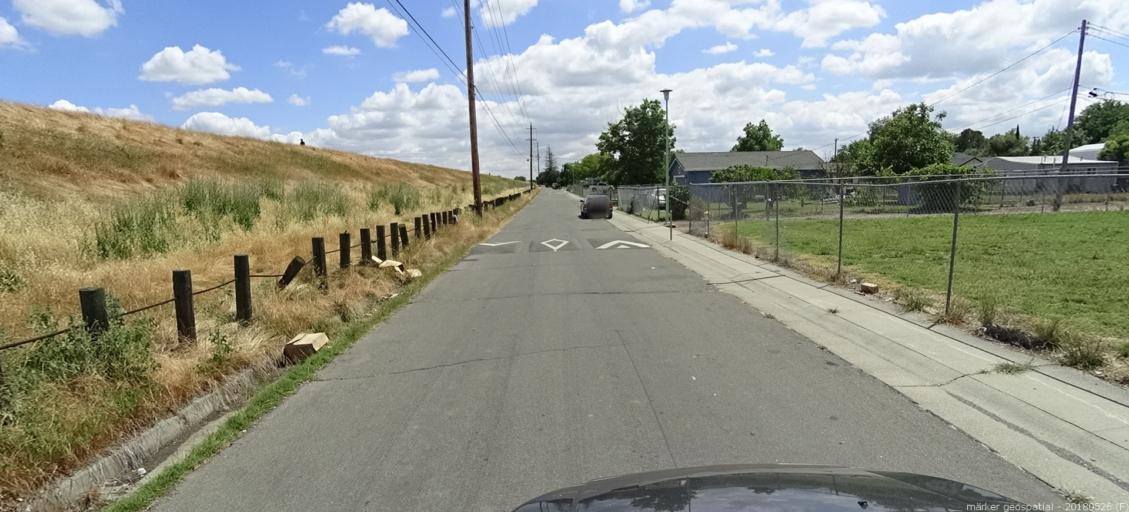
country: US
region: California
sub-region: Sacramento County
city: Sacramento
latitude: 38.6227
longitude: -121.4702
